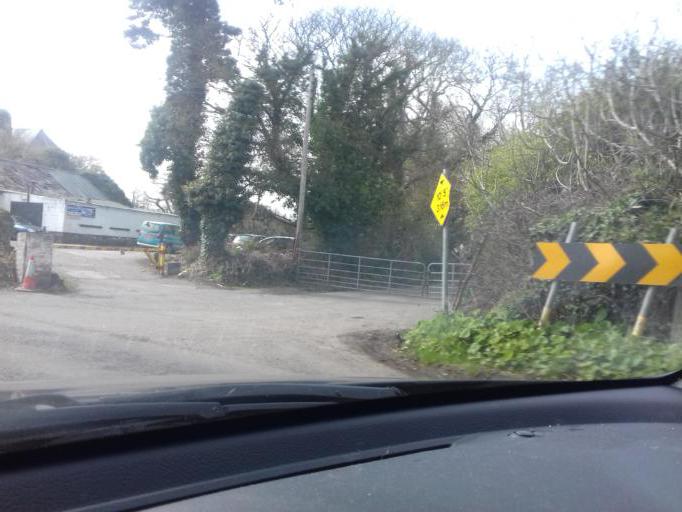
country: IE
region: Leinster
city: Portmarnock
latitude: 53.4280
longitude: -6.1542
